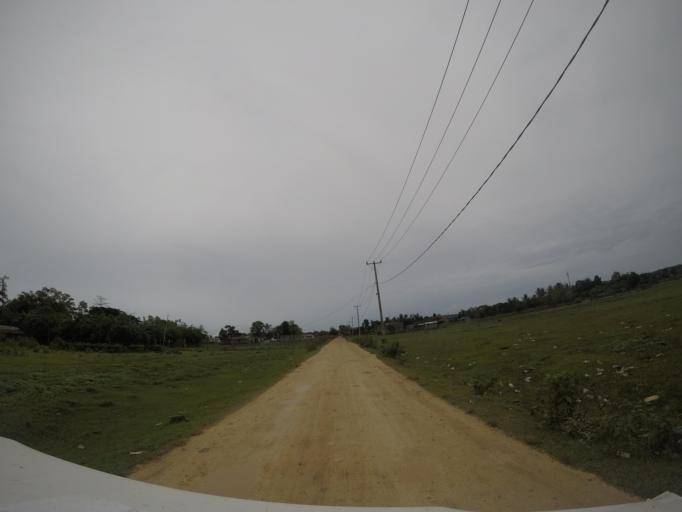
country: TL
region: Lautem
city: Lospalos
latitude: -8.5234
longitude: 127.0042
